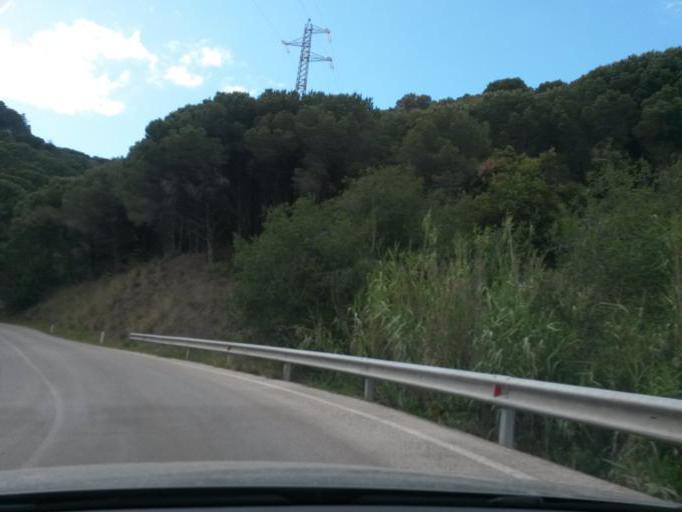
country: IT
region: Tuscany
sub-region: Provincia di Livorno
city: Rio nell'Elba
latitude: 42.7891
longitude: 10.4051
